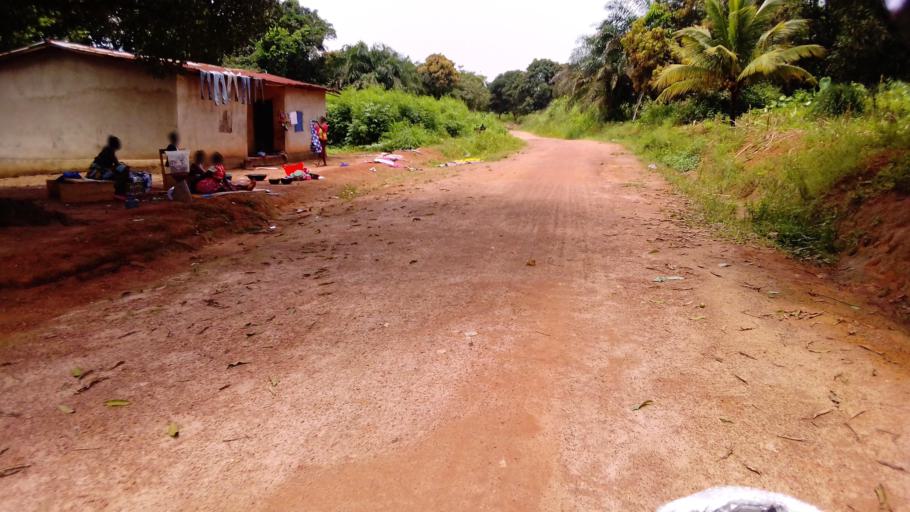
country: SL
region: Eastern Province
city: Koidu
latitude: 8.6608
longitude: -10.9413
